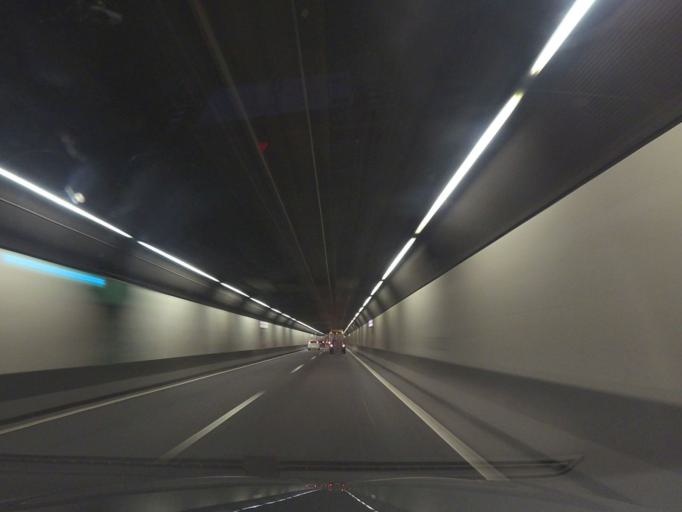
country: NL
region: North Holland
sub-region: Gemeente Velsen
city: Velsen-Zuid
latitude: 52.4651
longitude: 4.6531
